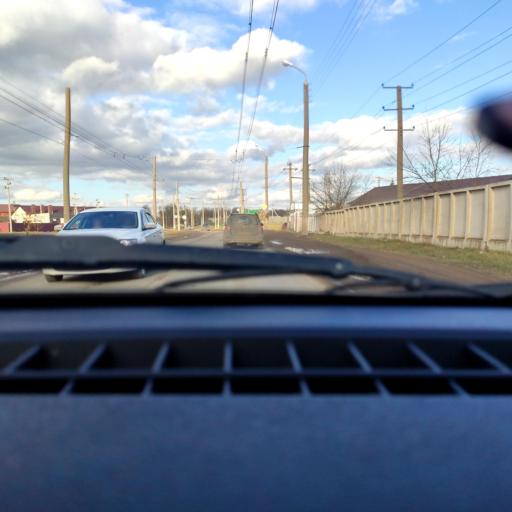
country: RU
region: Bashkortostan
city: Ufa
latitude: 54.7841
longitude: 55.9487
